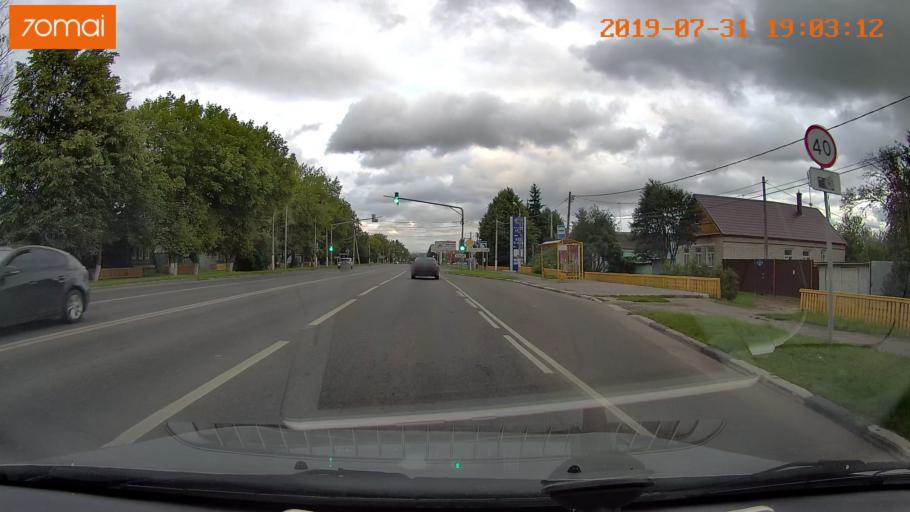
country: RU
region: Moskovskaya
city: Raduzhnyy
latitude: 55.1163
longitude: 38.7364
